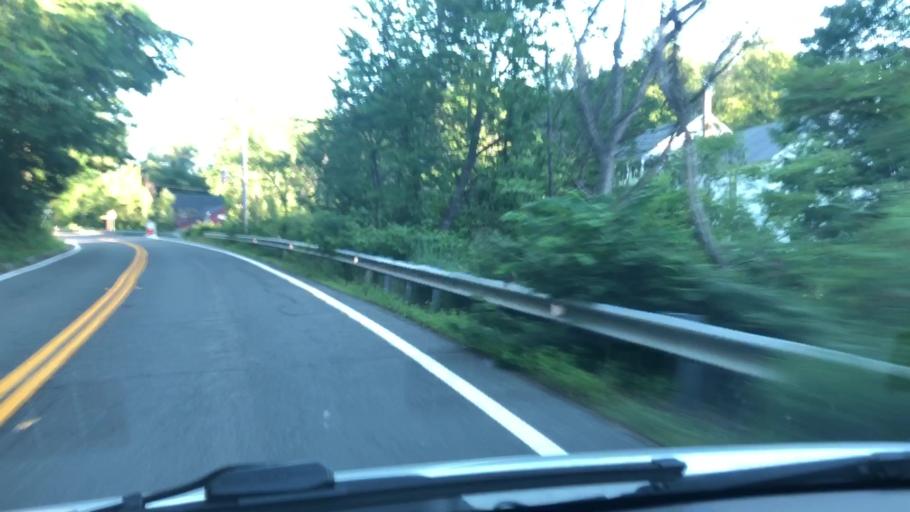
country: US
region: Massachusetts
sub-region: Hampshire County
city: Chesterfield
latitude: 42.3428
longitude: -72.8890
